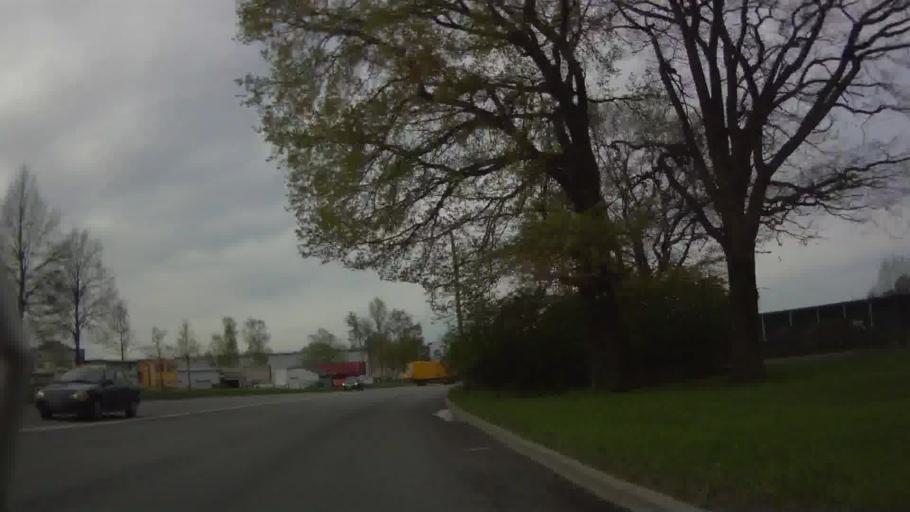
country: LV
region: Stopini
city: Ulbroka
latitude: 56.9568
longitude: 24.2275
